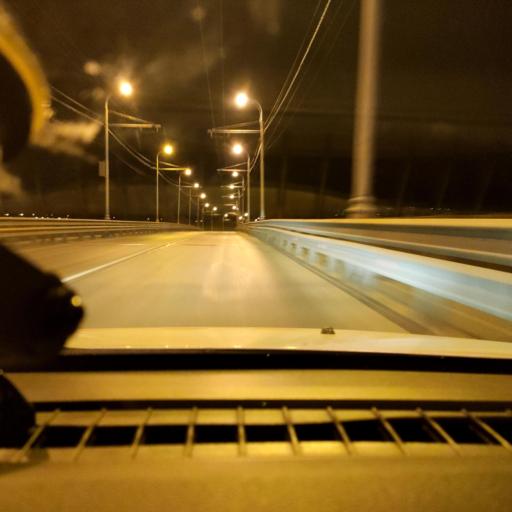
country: RU
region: Samara
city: Rozhdestveno
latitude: 53.1727
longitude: 50.0745
